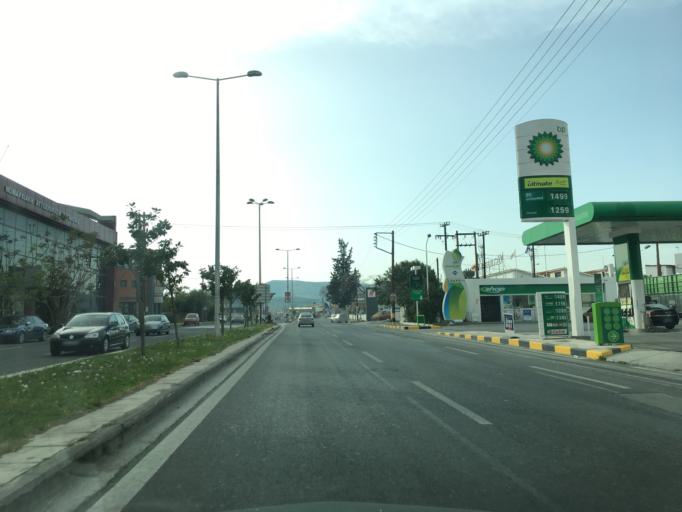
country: GR
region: Thessaly
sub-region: Nomos Magnisias
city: Nea Ionia
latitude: 39.3675
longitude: 22.9218
